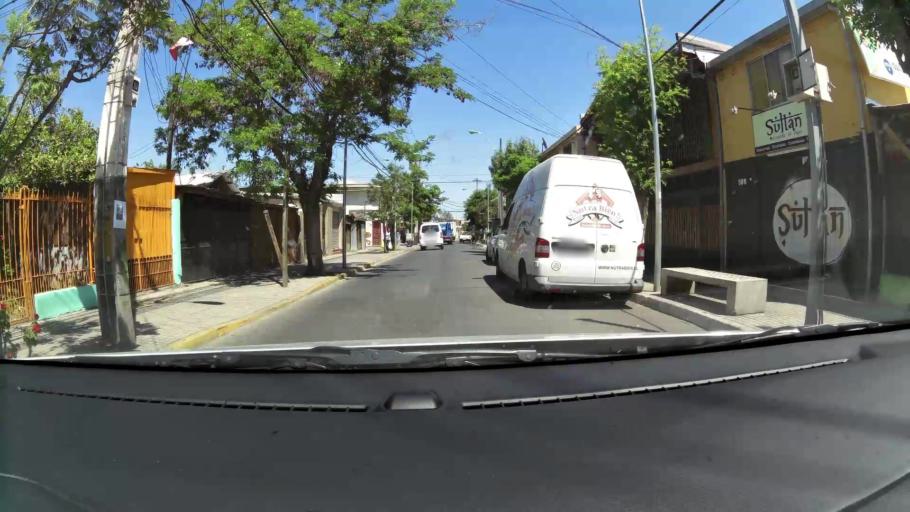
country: CL
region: Santiago Metropolitan
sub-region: Provincia de Maipo
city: San Bernardo
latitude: -33.5656
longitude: -70.6771
